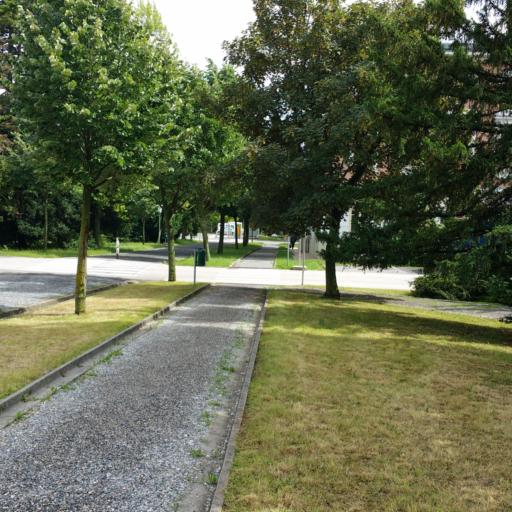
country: AT
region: Lower Austria
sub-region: Politischer Bezirk Modling
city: Perchtoldsdorf
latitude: 48.2082
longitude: 16.2805
